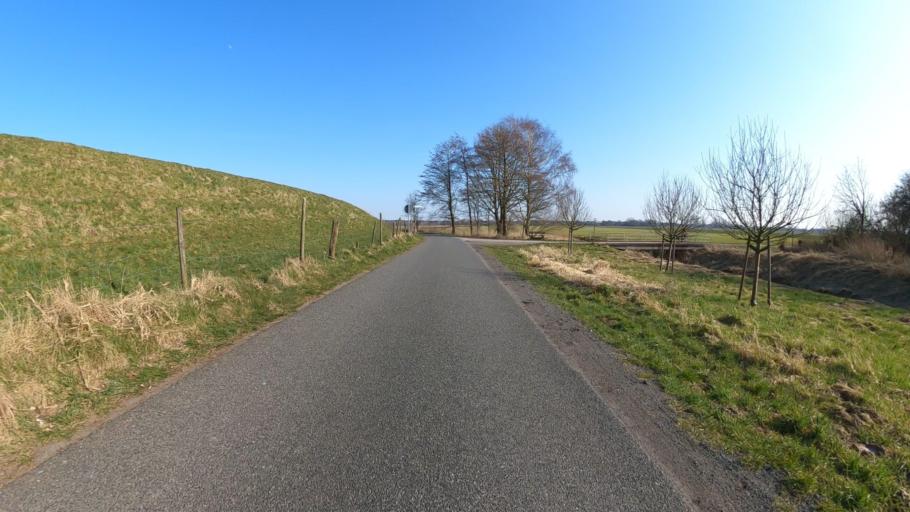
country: DE
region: Schleswig-Holstein
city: Seester
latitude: 53.7359
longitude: 9.6138
